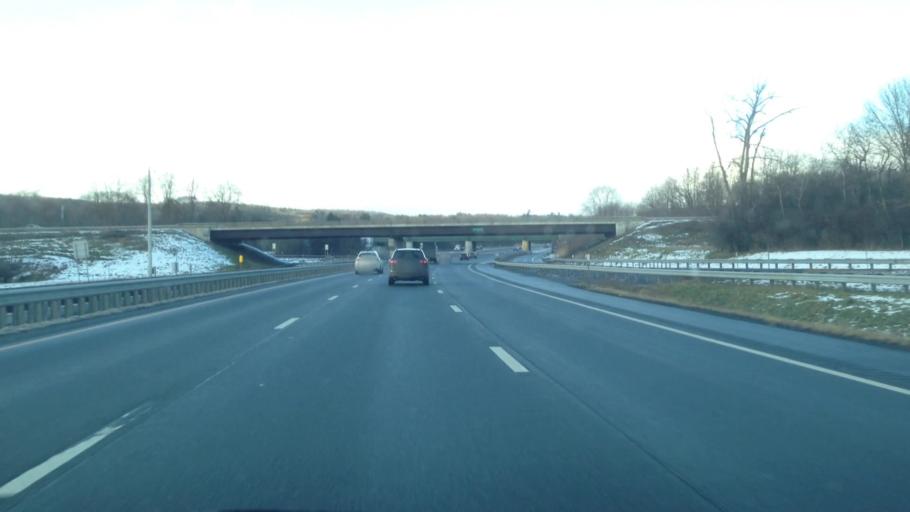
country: US
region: New York
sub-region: Schenectady County
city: Rotterdam
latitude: 42.7890
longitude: -74.0153
